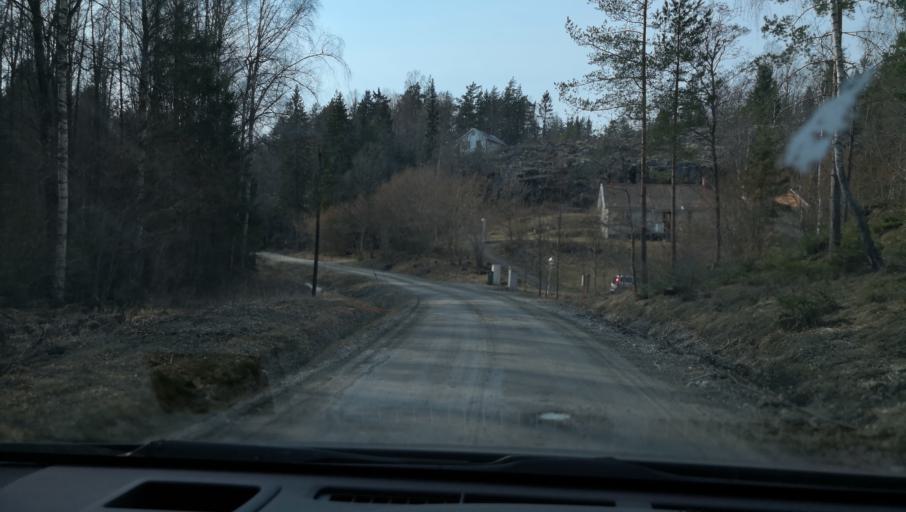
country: SE
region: OErebro
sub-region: Lindesbergs Kommun
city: Frovi
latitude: 59.3902
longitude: 15.4005
